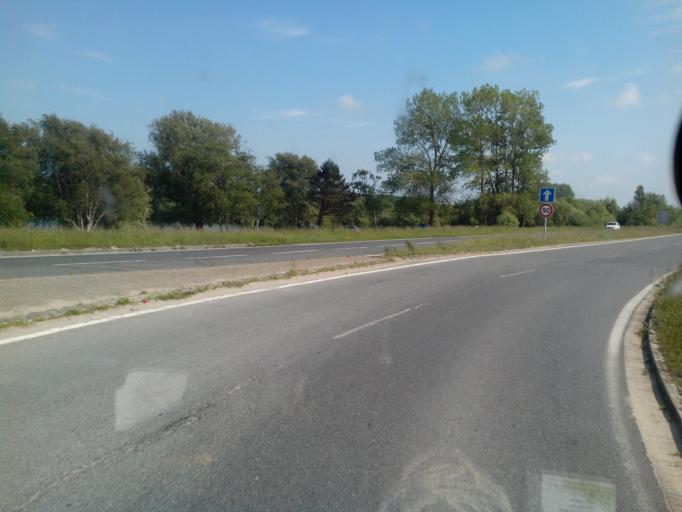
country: FR
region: Picardie
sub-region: Departement de la Somme
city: Quend
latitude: 50.2945
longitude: 1.6505
